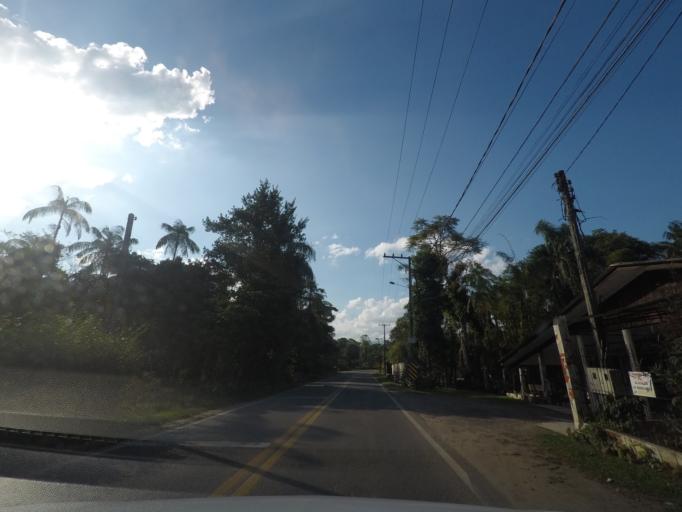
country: BR
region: Parana
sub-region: Antonina
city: Antonina
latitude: -25.4360
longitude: -48.8761
